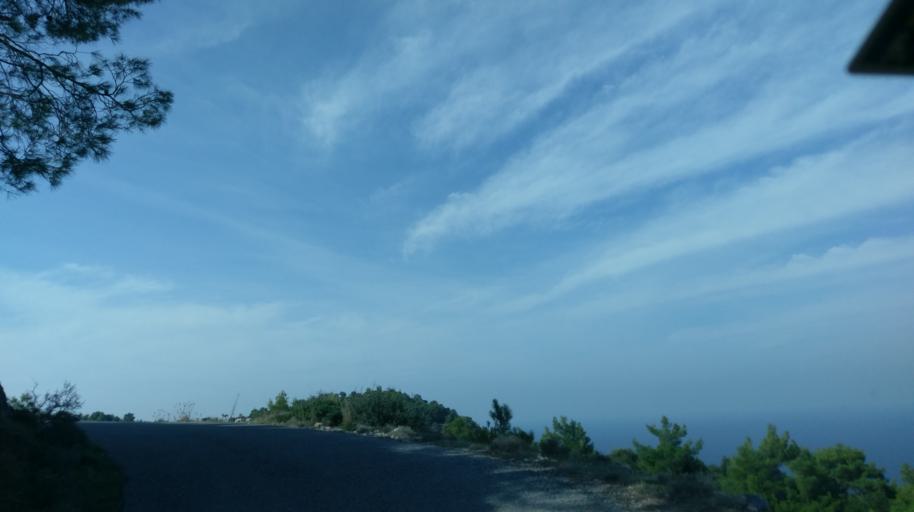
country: CY
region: Keryneia
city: Lapithos
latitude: 35.3393
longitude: 33.1104
